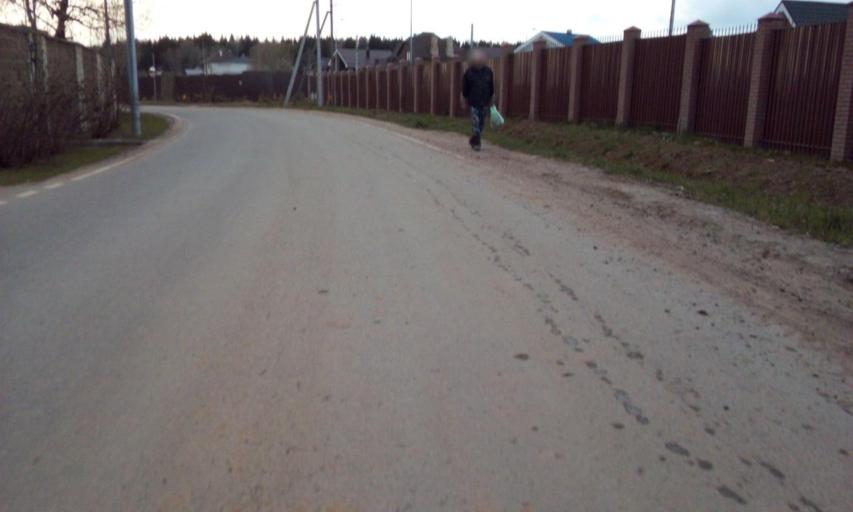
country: RU
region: Moskovskaya
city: Troitsk
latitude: 55.5247
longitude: 37.2643
